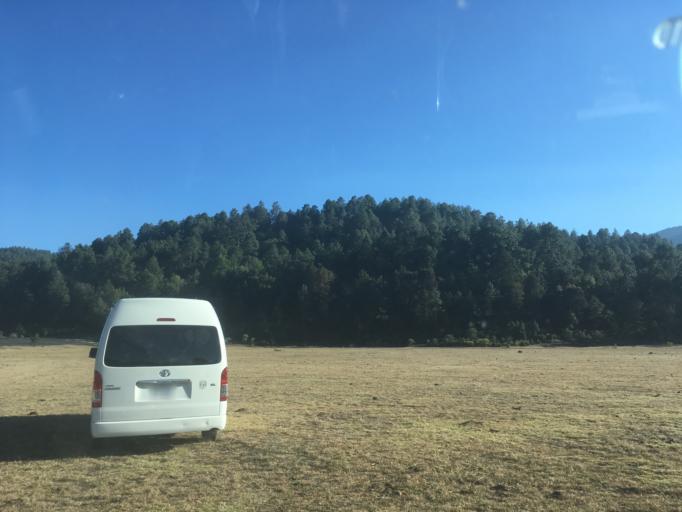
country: MX
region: Michoacan
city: Angahuan
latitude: 19.4844
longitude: -102.2537
